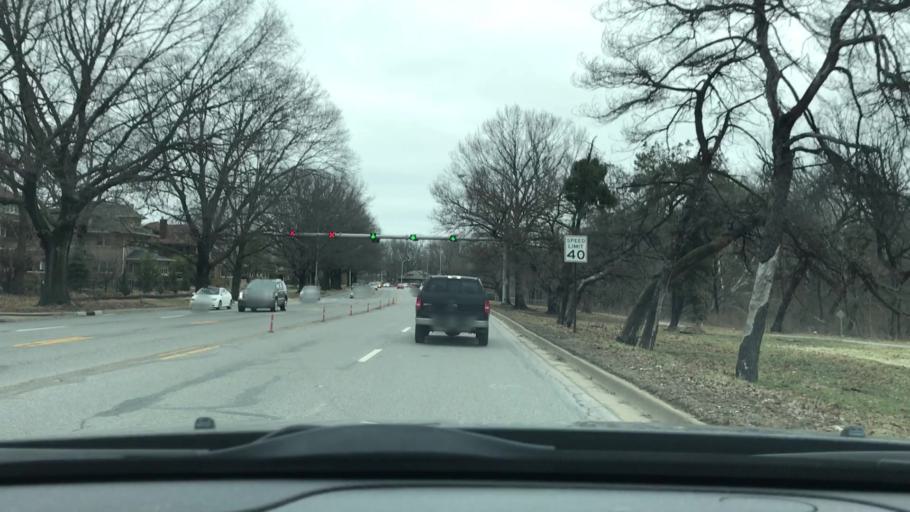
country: US
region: Indiana
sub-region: Marion County
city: Indianapolis
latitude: 39.8109
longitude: -86.1436
